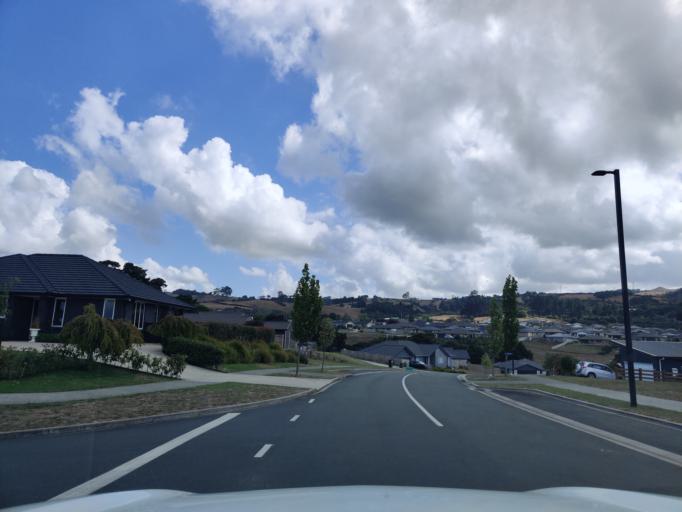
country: NZ
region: Auckland
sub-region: Auckland
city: Pukekohe East
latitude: -37.2354
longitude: 175.0102
